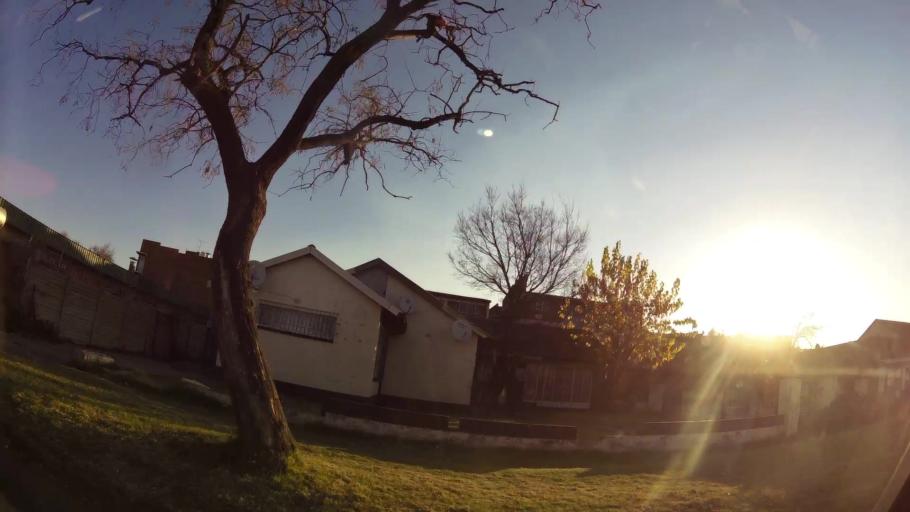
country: ZA
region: Gauteng
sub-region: Ekurhuleni Metropolitan Municipality
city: Germiston
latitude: -26.2729
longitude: 28.1235
